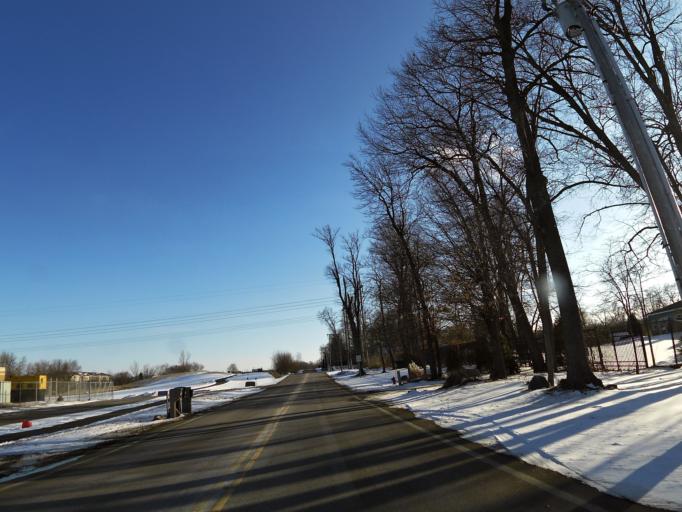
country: US
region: Minnesota
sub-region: Scott County
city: Prior Lake
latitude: 44.7546
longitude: -93.4495
